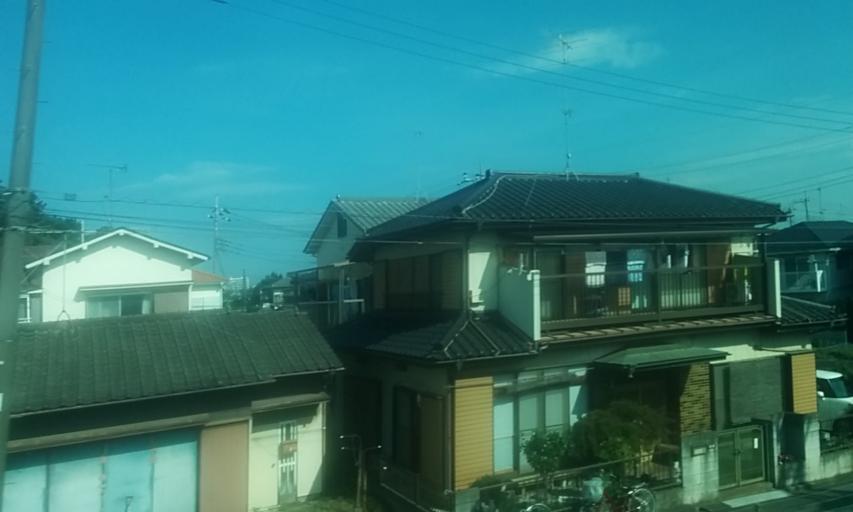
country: JP
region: Saitama
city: Hasuda
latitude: 35.9758
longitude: 139.6498
